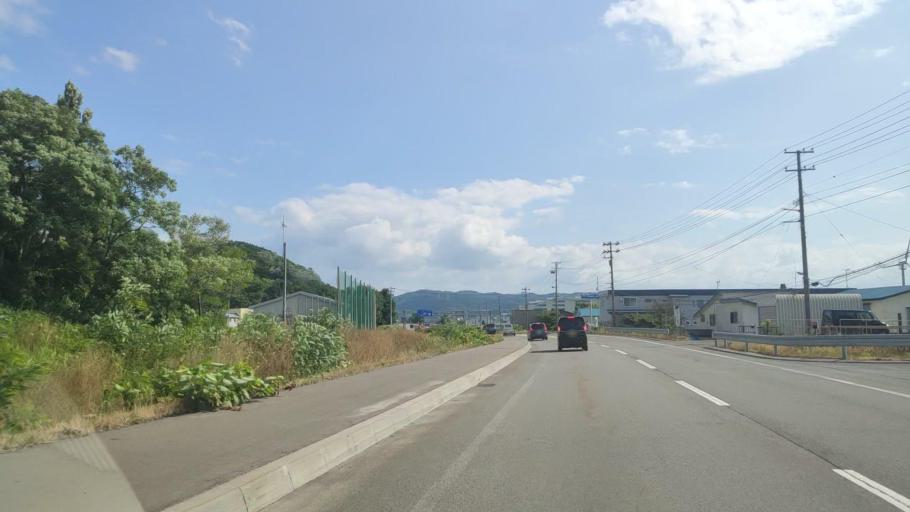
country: JP
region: Hokkaido
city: Rumoi
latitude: 43.9559
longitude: 141.6441
